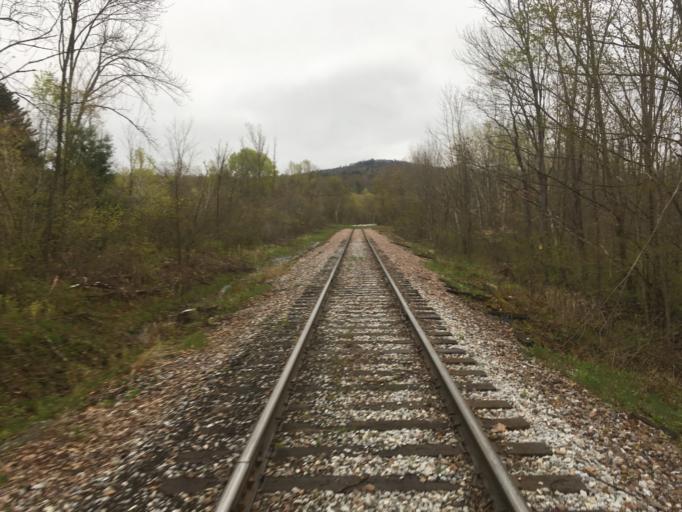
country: US
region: Vermont
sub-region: Rutland County
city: Rutland
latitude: 43.4779
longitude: -72.8742
